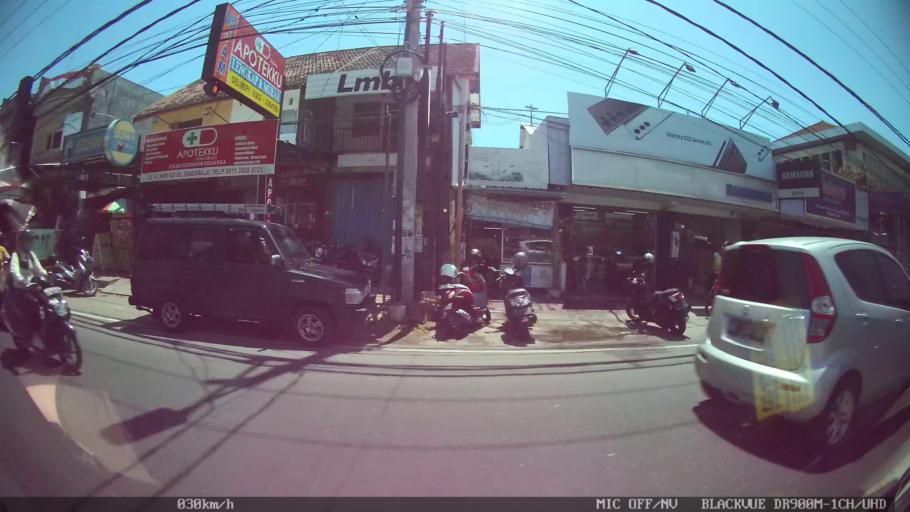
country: ID
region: Bali
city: Singaraja
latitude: -8.1117
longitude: 115.0859
